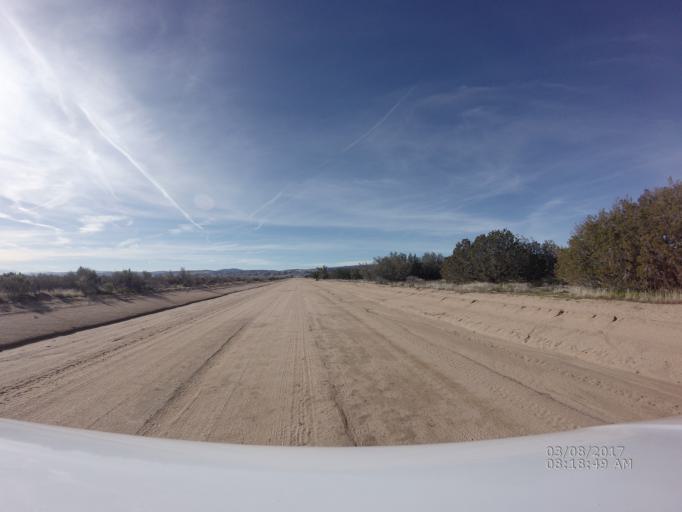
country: US
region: California
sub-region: Los Angeles County
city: Green Valley
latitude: 34.7652
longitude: -118.4489
